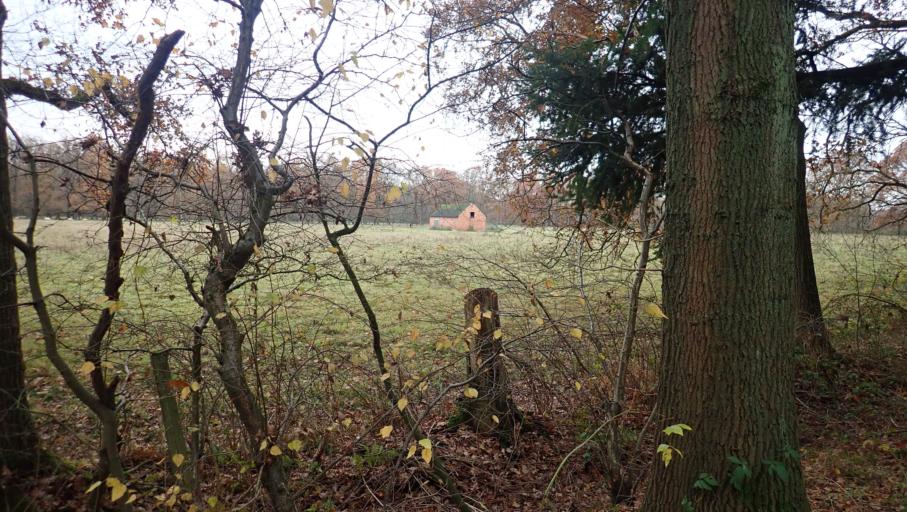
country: BE
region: Flanders
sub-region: Provincie Antwerpen
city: Hulshout
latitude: 51.0887
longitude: 4.7923
